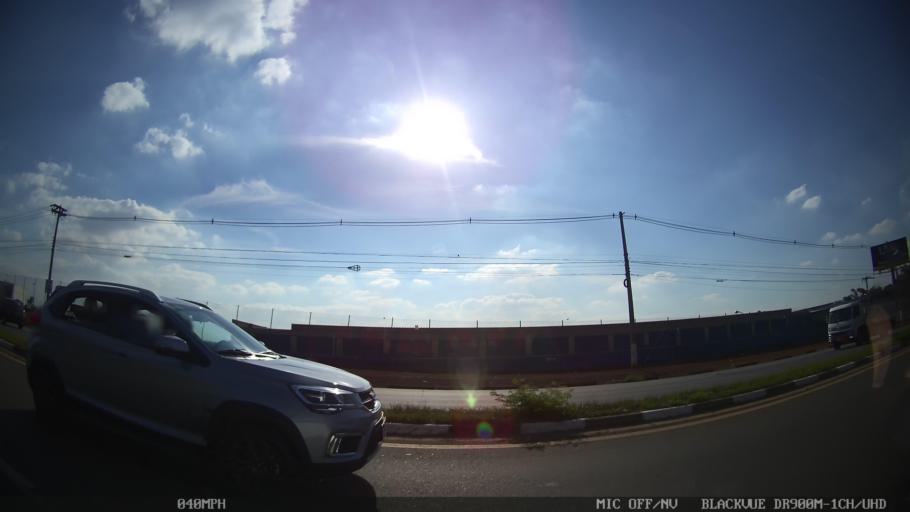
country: BR
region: Sao Paulo
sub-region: Hortolandia
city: Hortolandia
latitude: -22.8249
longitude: -47.1991
